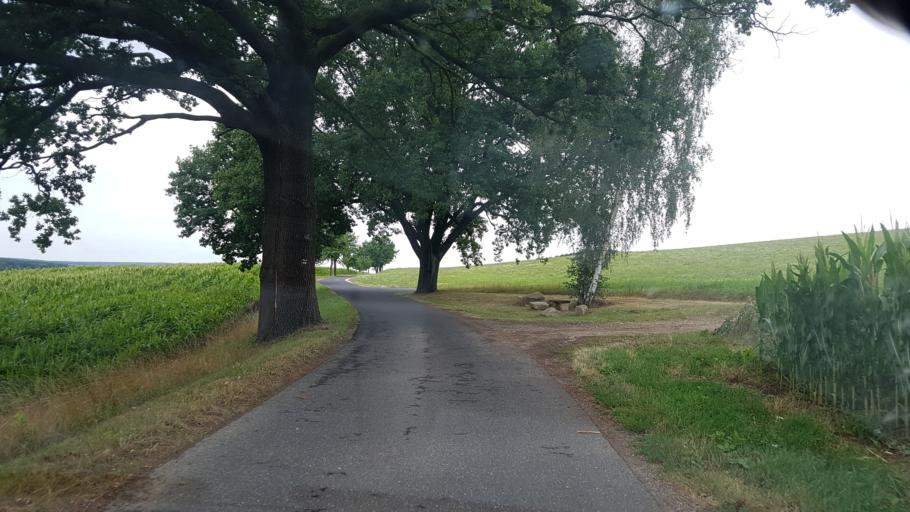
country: DE
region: Saxony
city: Kodersdorf
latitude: 51.2227
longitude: 14.8832
